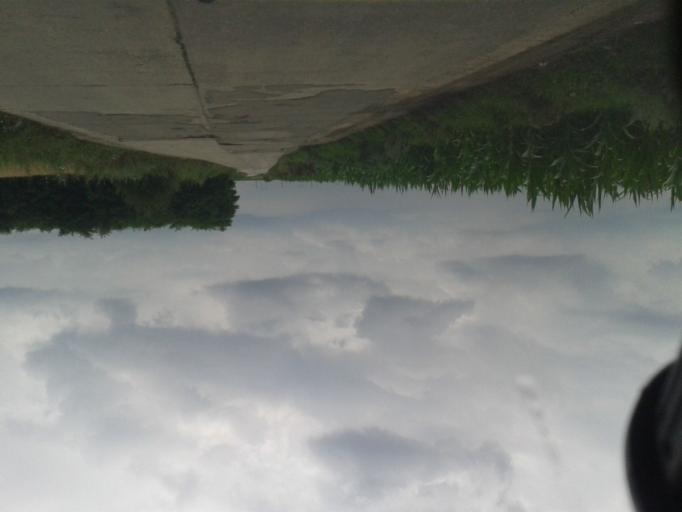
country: RO
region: Calarasi
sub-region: Comuna Fundulea
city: Fundulea
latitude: 44.4878
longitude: 26.5211
